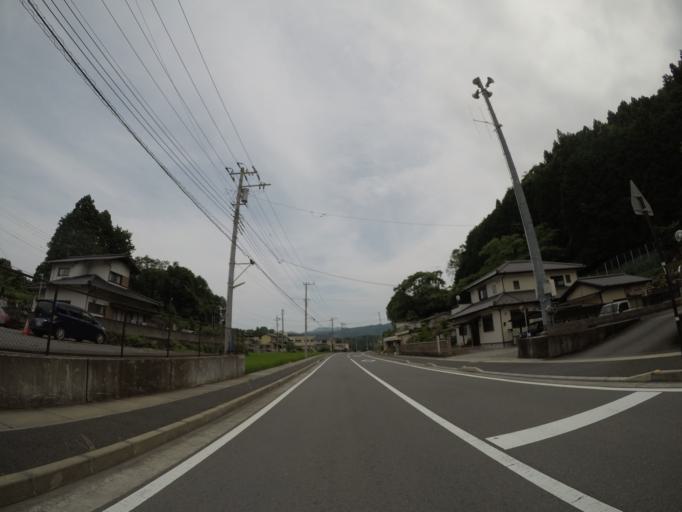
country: JP
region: Shizuoka
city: Fujinomiya
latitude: 35.2081
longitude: 138.5654
